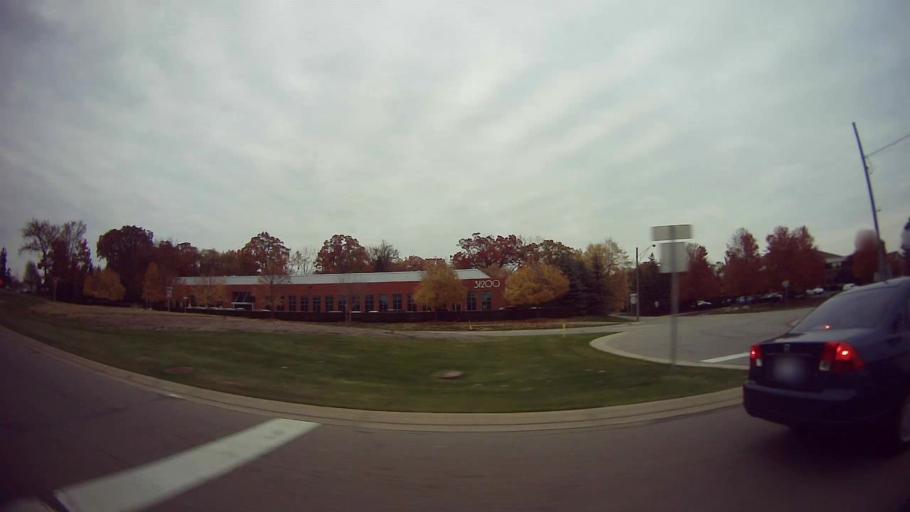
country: US
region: Michigan
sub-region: Oakland County
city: Franklin
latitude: 42.5155
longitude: -83.3346
